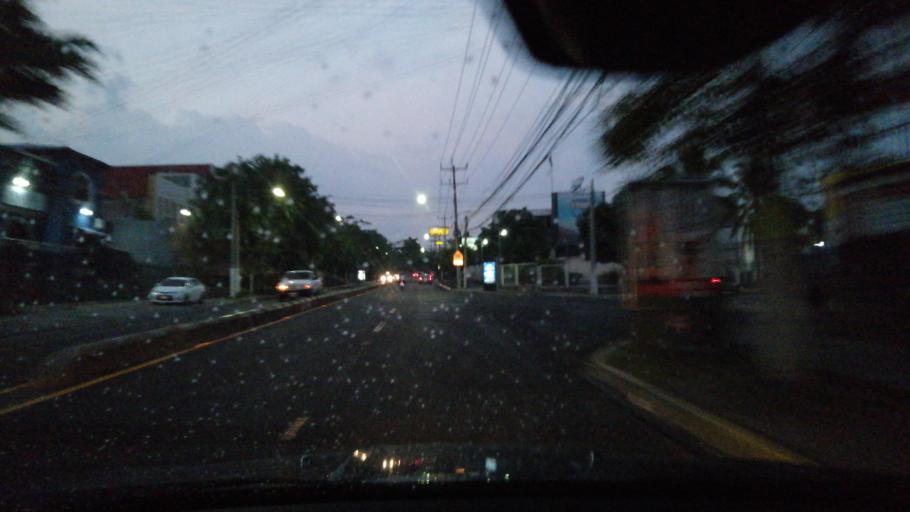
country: SV
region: San Salvador
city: San Salvador
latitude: 13.7074
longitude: -89.2041
